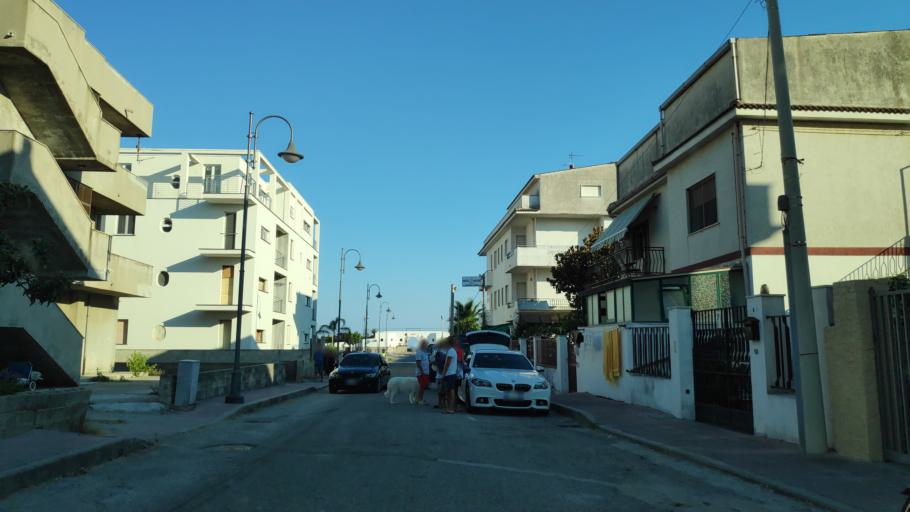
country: IT
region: Calabria
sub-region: Provincia di Reggio Calabria
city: Caulonia Marina
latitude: 38.3409
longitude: 16.4636
